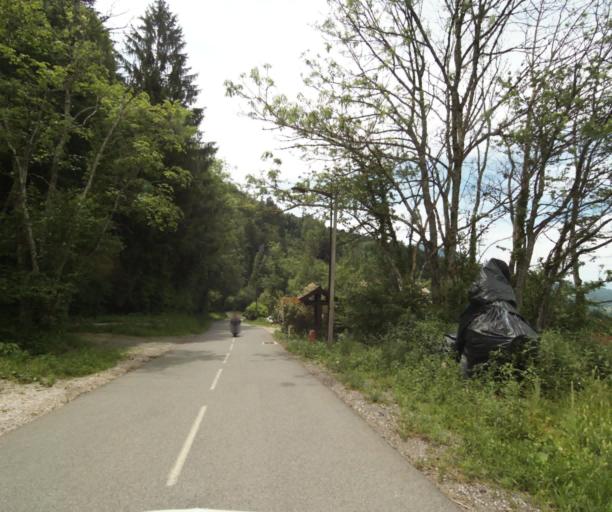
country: FR
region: Rhone-Alpes
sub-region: Departement de la Haute-Savoie
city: Bons-en-Chablais
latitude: 46.2645
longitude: 6.4174
